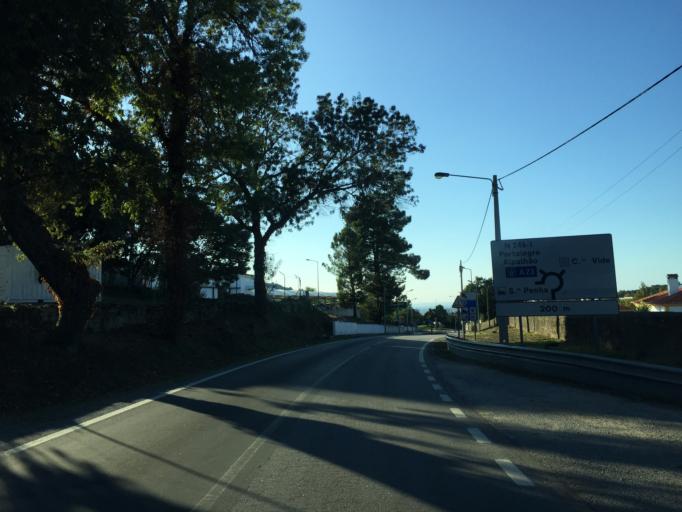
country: PT
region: Portalegre
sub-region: Castelo de Vide
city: Castelo de Vide
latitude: 39.4049
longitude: -7.4430
